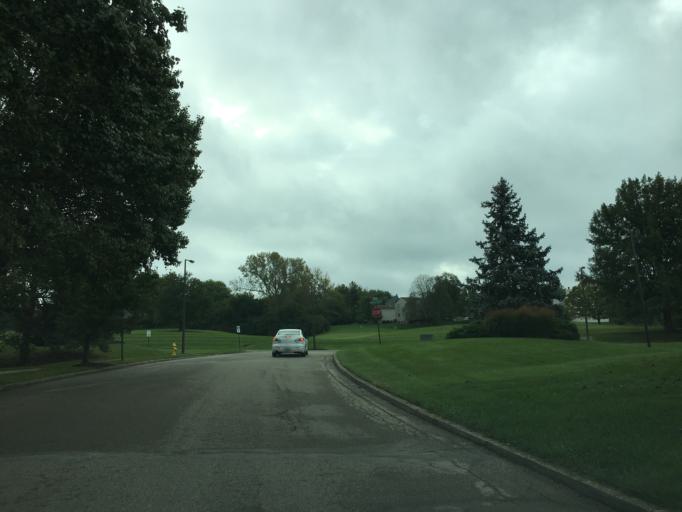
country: US
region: Ohio
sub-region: Butler County
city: Beckett Ridge
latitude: 39.3530
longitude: -84.4496
